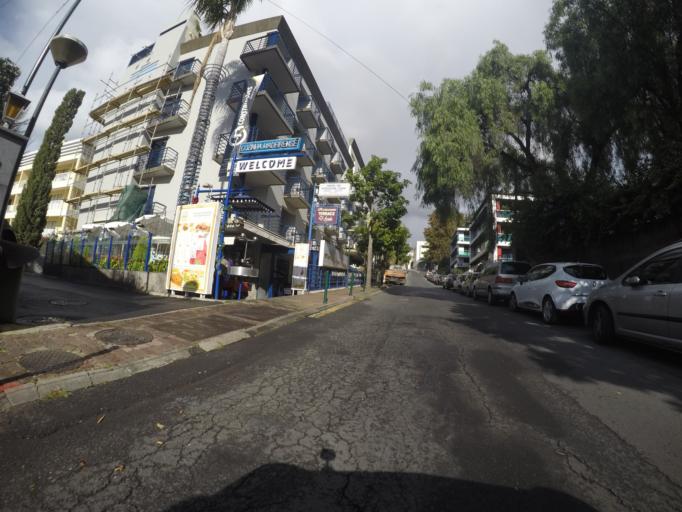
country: PT
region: Madeira
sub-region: Funchal
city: Funchal
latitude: 32.6395
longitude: -16.9274
